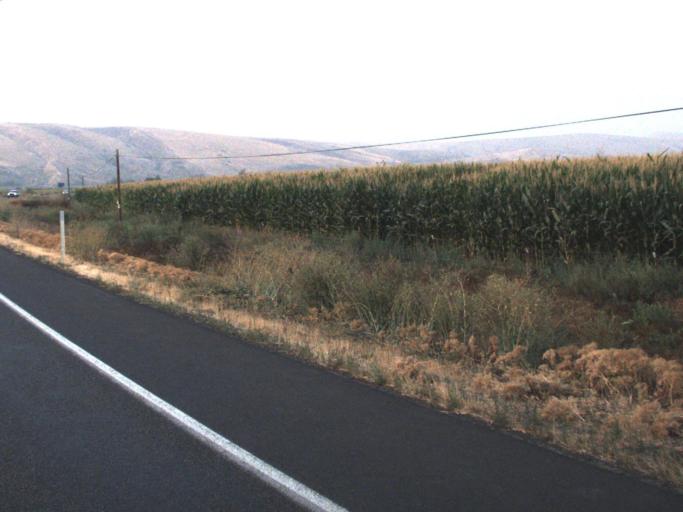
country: US
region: Washington
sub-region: Yakima County
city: Toppenish
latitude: 46.3221
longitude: -120.3206
